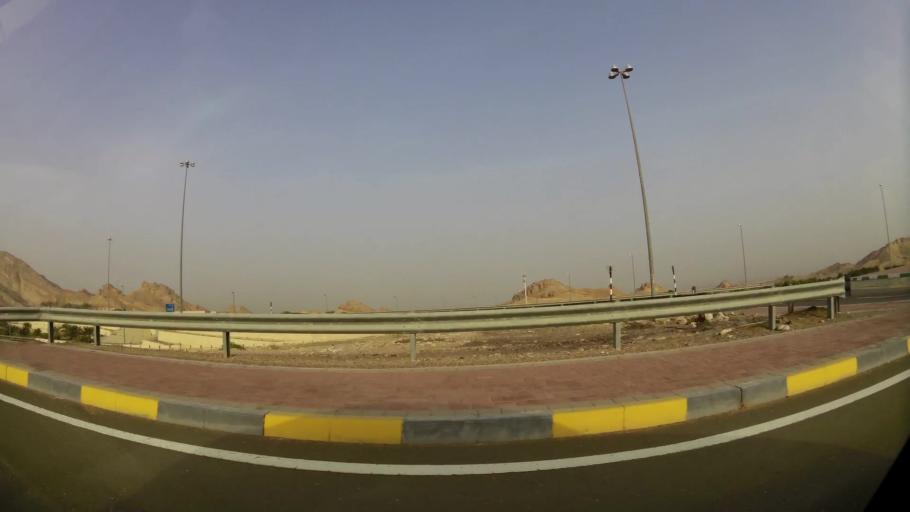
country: AE
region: Abu Dhabi
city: Al Ain
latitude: 24.1132
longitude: 55.7540
